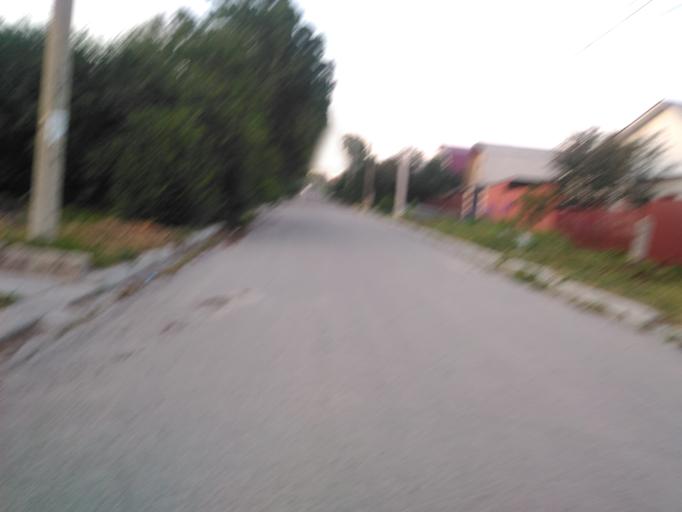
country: RU
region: Ulyanovsk
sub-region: Ulyanovskiy Rayon
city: Ulyanovsk
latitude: 54.3367
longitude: 48.3633
